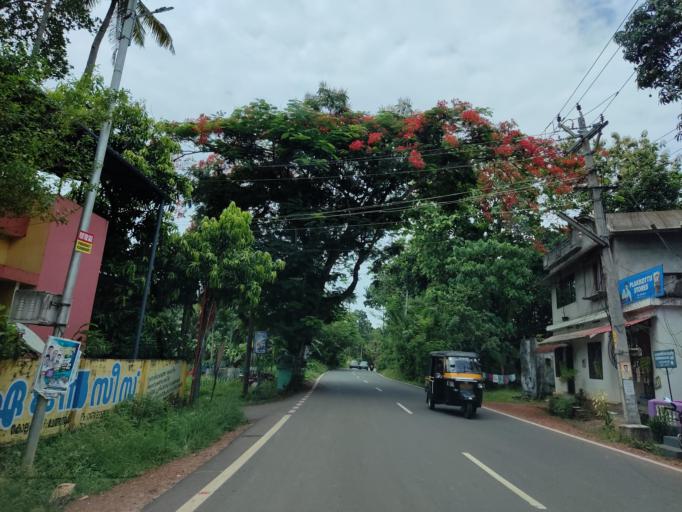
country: IN
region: Kerala
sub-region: Alappuzha
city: Chengannur
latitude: 9.2681
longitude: 76.6065
